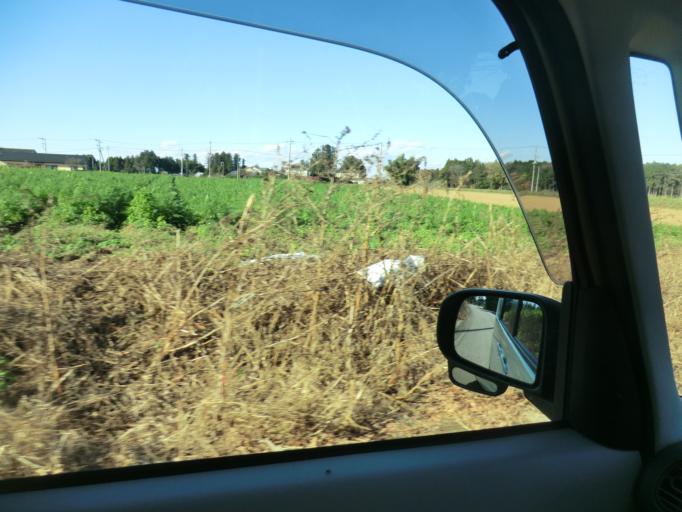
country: JP
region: Ibaraki
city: Okunoya
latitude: 36.1966
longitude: 140.4012
